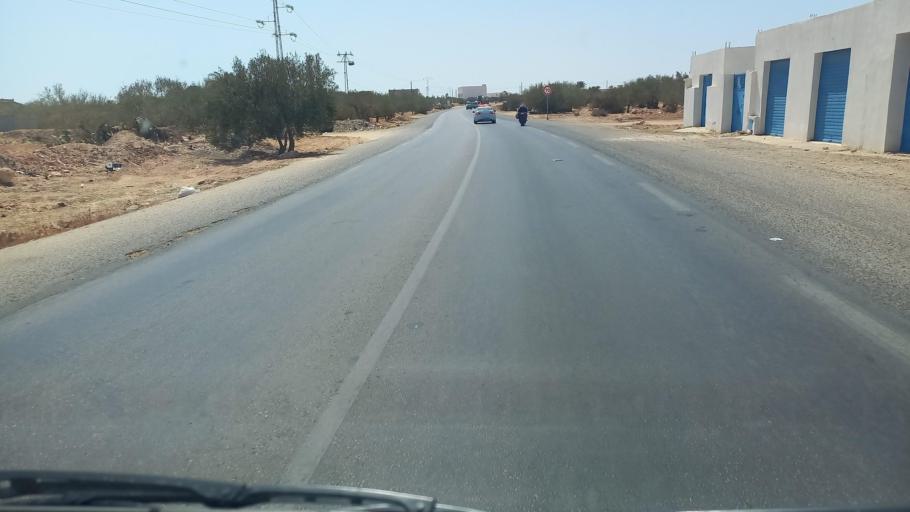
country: TN
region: Madanin
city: Houmt Souk
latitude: 33.8215
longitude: 10.8706
